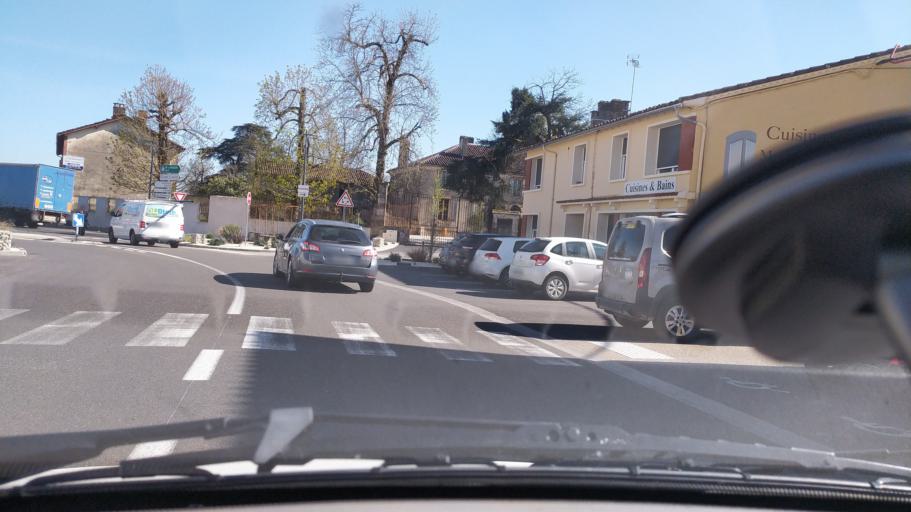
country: FR
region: Midi-Pyrenees
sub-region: Departement du Gers
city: Nogaro
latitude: 43.7576
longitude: -0.0330
